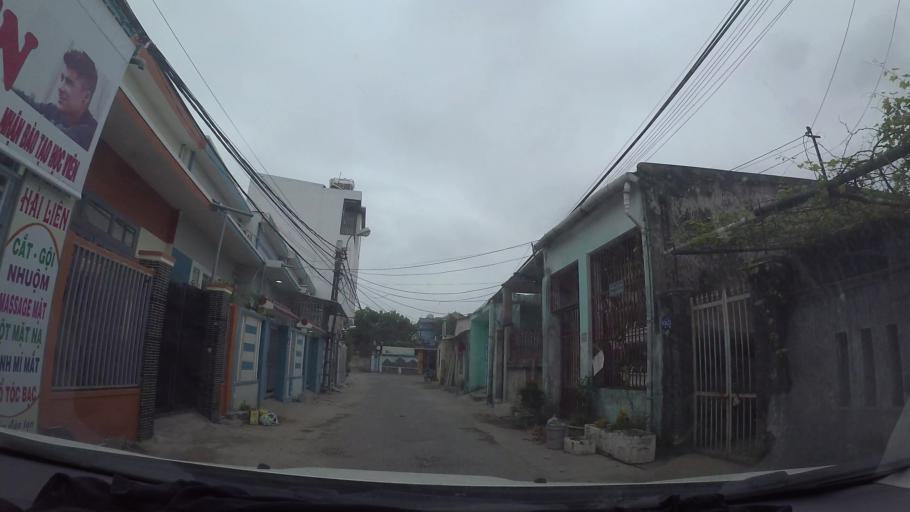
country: VN
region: Da Nang
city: Lien Chieu
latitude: 16.0853
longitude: 108.1430
